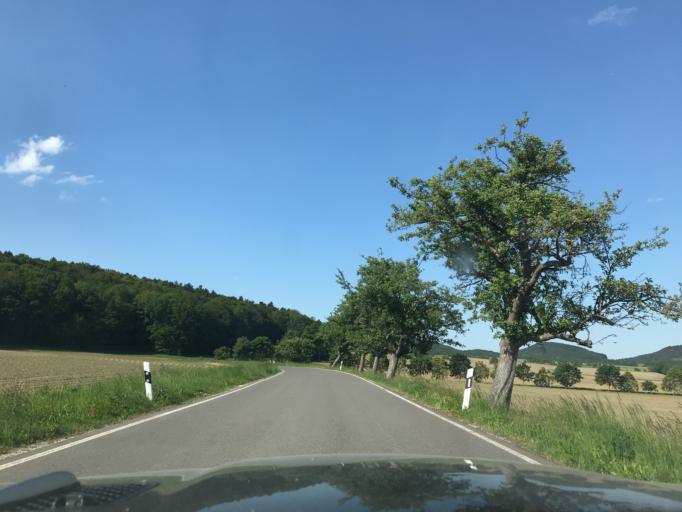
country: DE
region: Thuringia
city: Plaue
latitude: 50.7590
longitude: 10.9464
